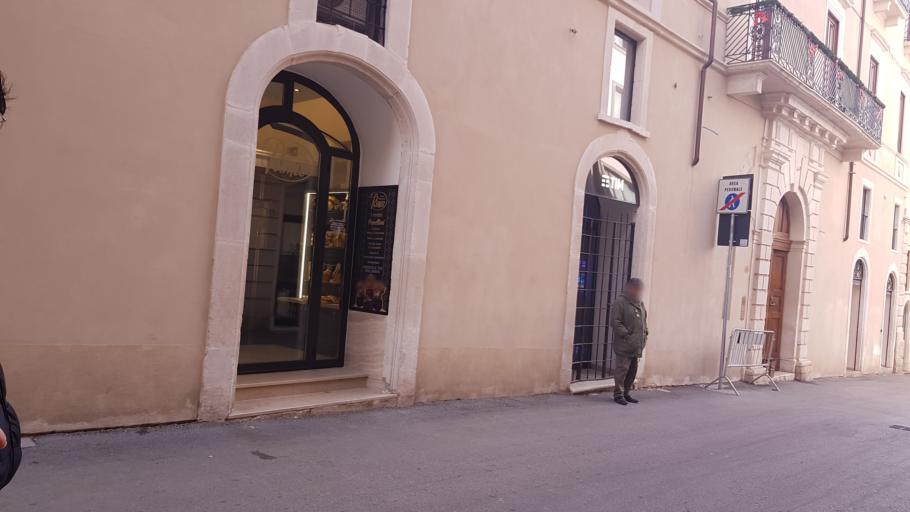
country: IT
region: Abruzzo
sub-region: Provincia dell' Aquila
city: L'Aquila
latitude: 42.3475
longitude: 13.3982
